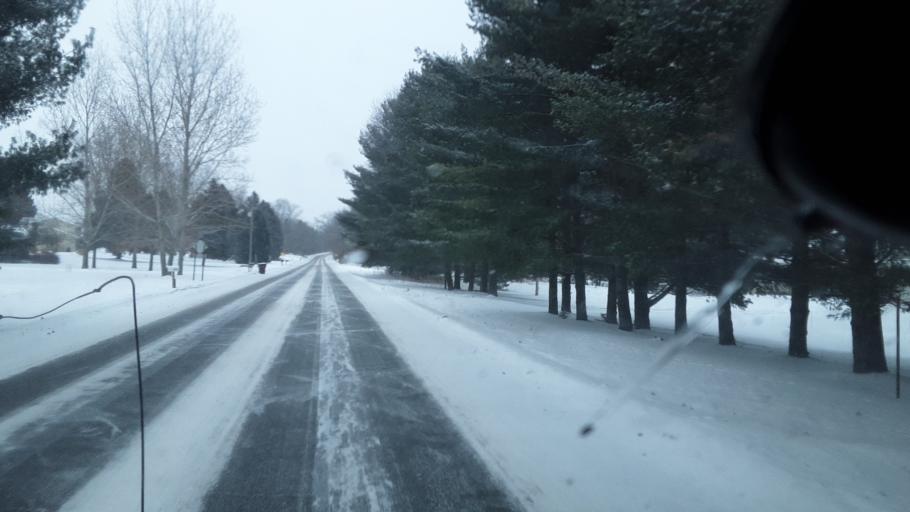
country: US
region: Michigan
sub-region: Ingham County
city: Mason
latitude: 42.5479
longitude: -84.3733
